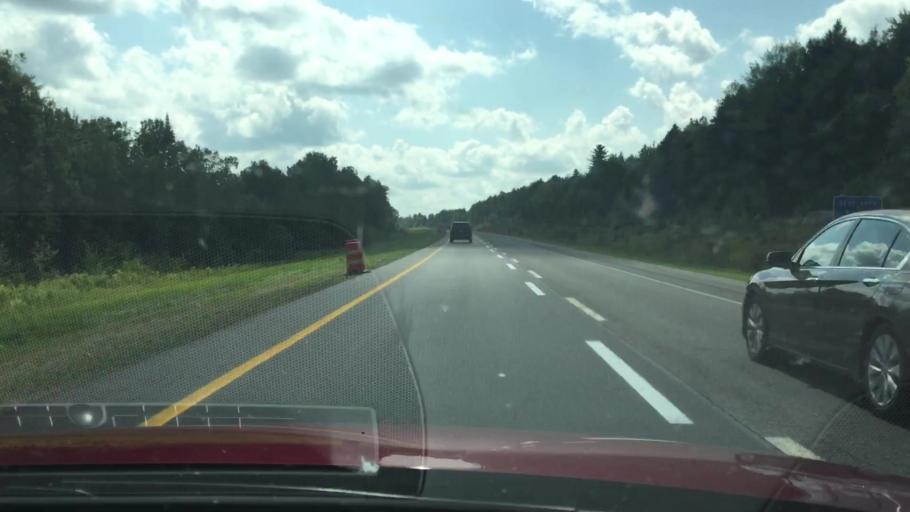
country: US
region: Maine
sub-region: Penobscot County
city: Medway
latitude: 45.6354
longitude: -68.5026
